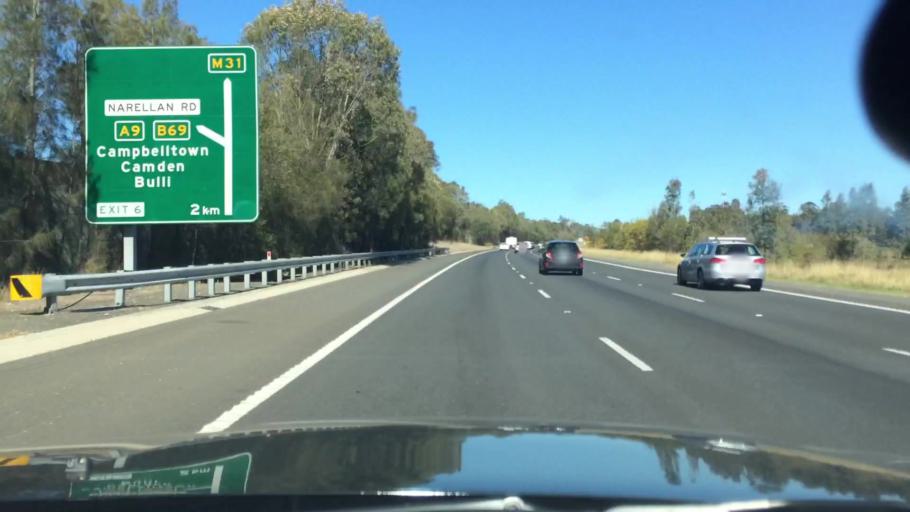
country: AU
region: New South Wales
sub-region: Campbelltown Municipality
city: Leumeah
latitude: -34.0489
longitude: 150.8166
